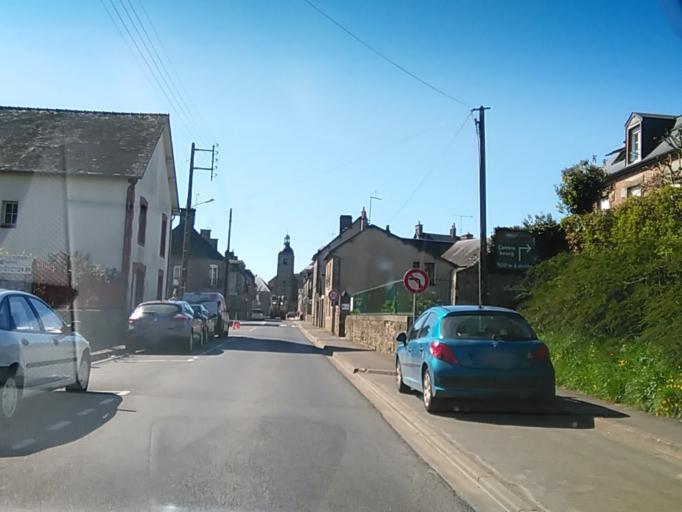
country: FR
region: Pays de la Loire
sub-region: Departement de la Mayenne
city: Pre-en-Pail
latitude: 48.5663
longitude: -0.1431
